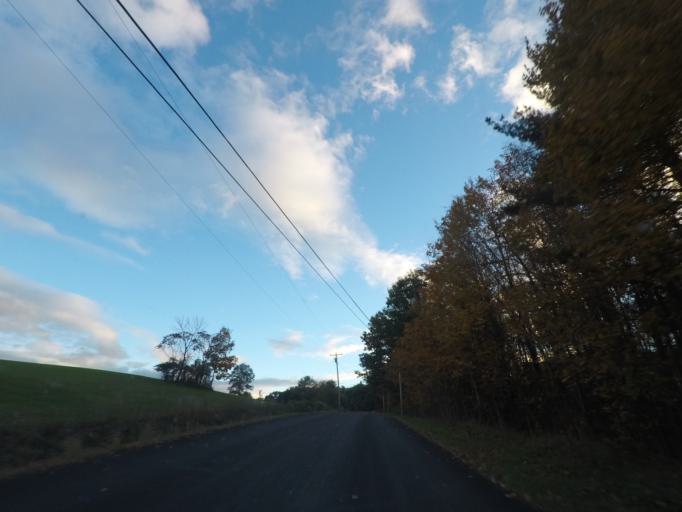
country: US
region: New York
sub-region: Rensselaer County
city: Nassau
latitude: 42.5243
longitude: -73.5900
